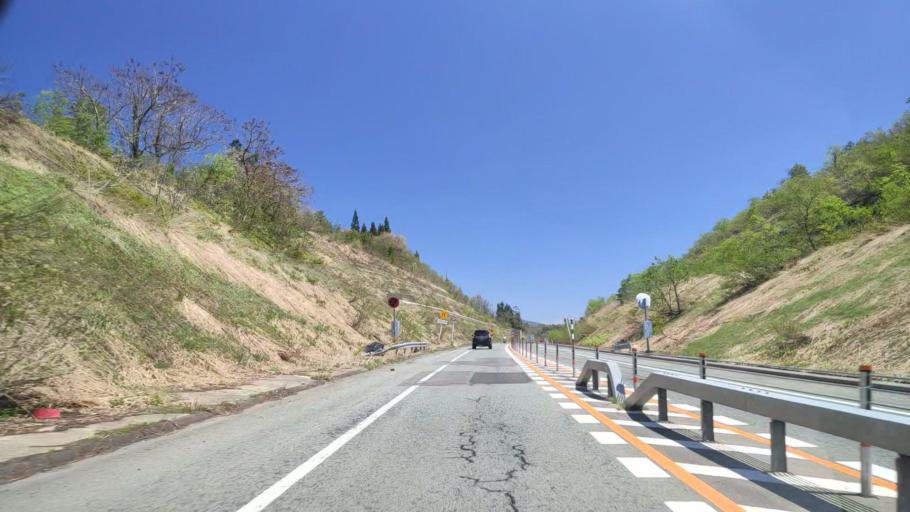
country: JP
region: Yamagata
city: Obanazawa
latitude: 38.6663
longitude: 140.3489
